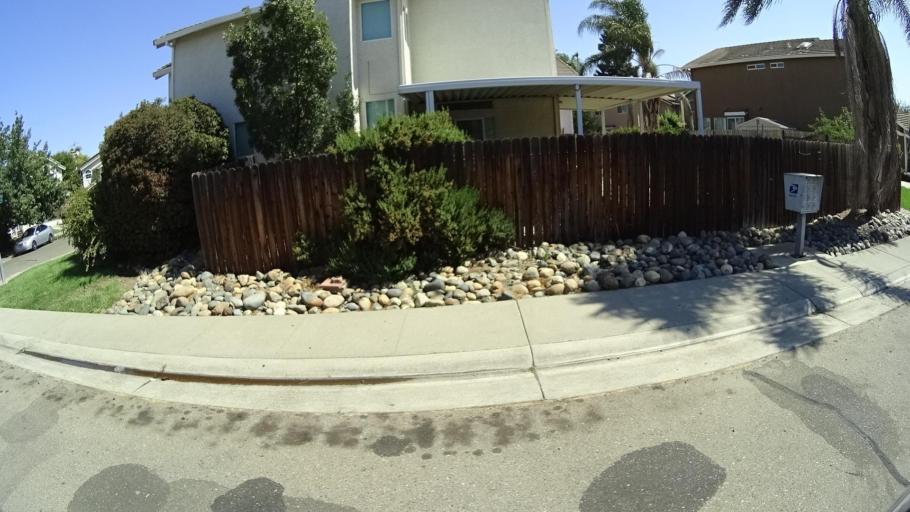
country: US
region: California
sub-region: Sacramento County
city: Laguna
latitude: 38.4215
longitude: -121.4139
